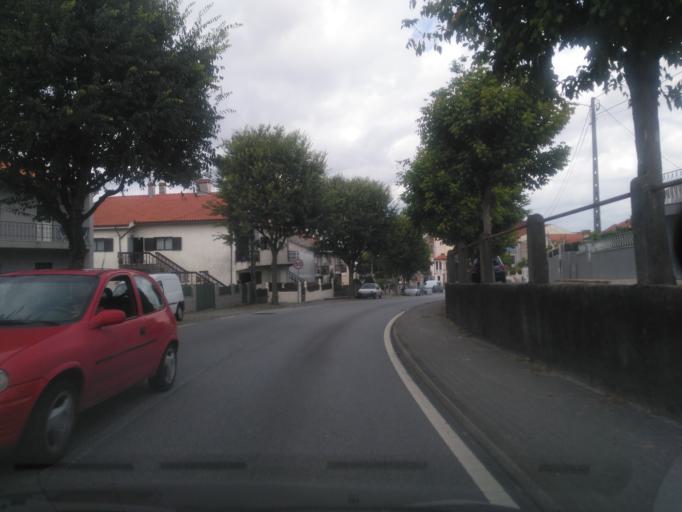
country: PT
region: Braga
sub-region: Braga
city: Braga
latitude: 41.5554
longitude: -8.4418
